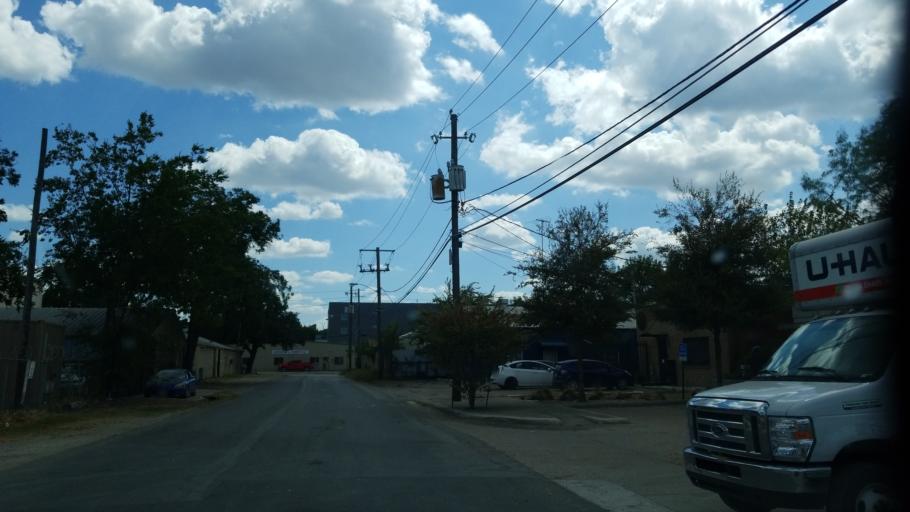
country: US
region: Texas
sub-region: Dallas County
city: Dallas
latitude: 32.7719
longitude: -96.8251
